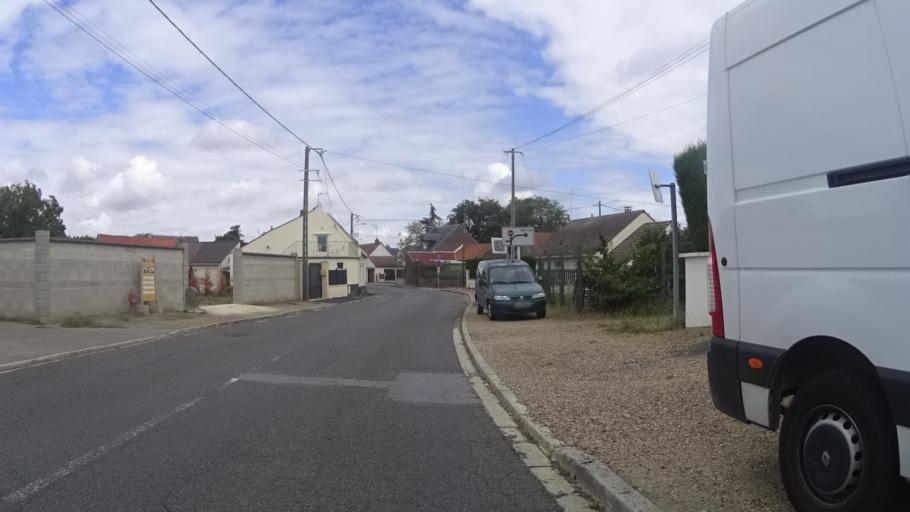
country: FR
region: Picardie
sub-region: Departement de l'Oise
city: Noyon
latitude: 49.5572
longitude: 2.9924
